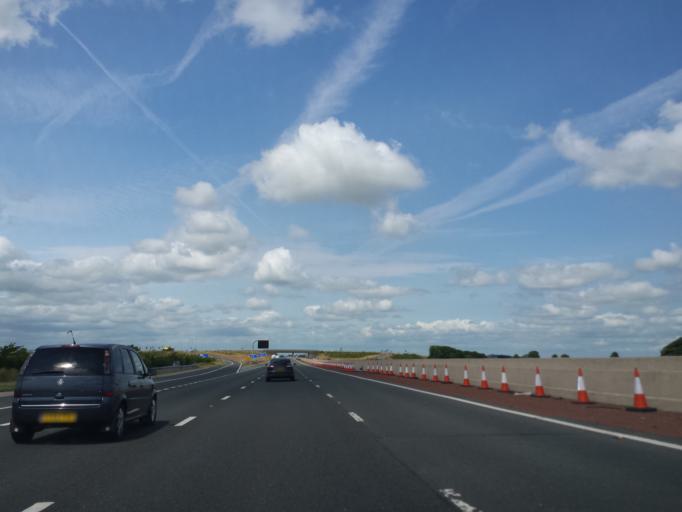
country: GB
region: England
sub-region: North Yorkshire
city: Ripon
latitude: 54.1759
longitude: -1.4547
